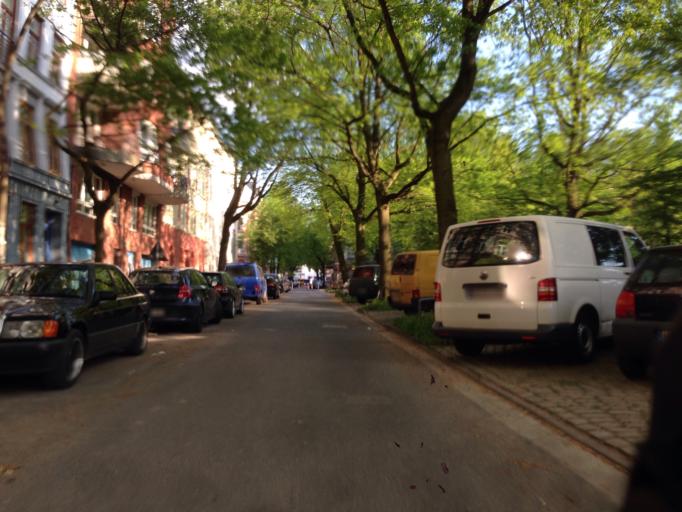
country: DE
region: Hamburg
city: Altona
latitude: 53.5603
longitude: 9.9464
